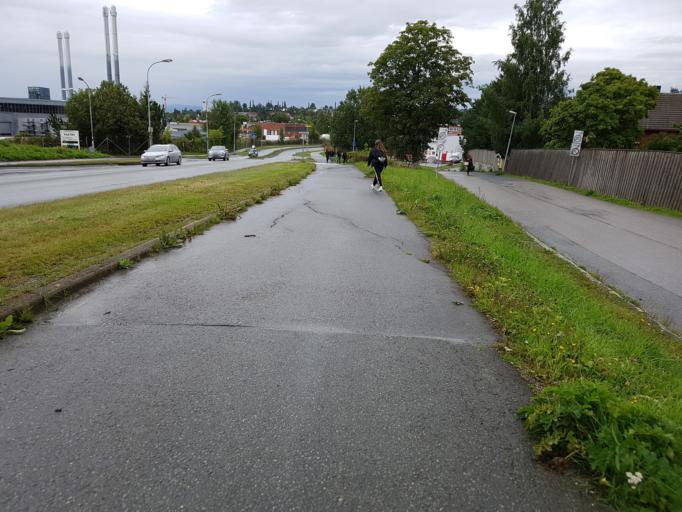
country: NO
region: Sor-Trondelag
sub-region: Trondheim
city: Trondheim
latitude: 63.3958
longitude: 10.4039
